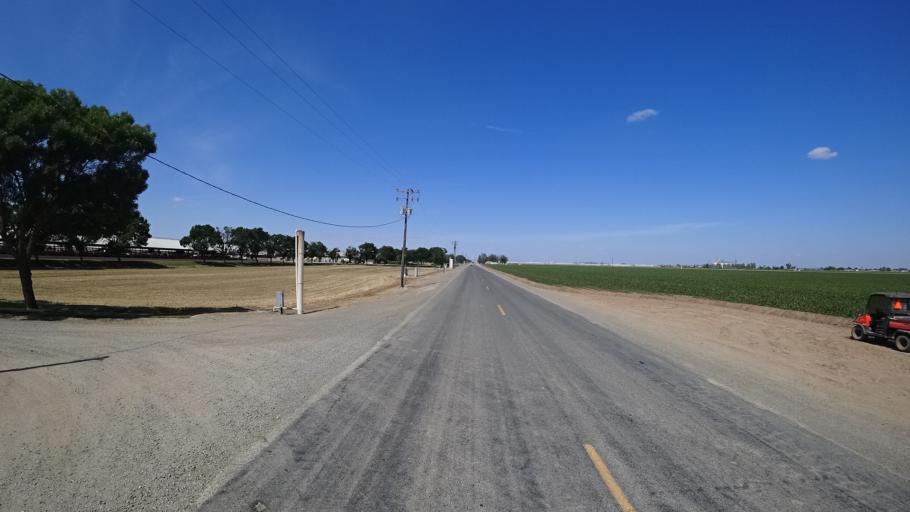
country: US
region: California
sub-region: Kings County
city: Home Garden
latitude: 36.2694
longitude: -119.6238
